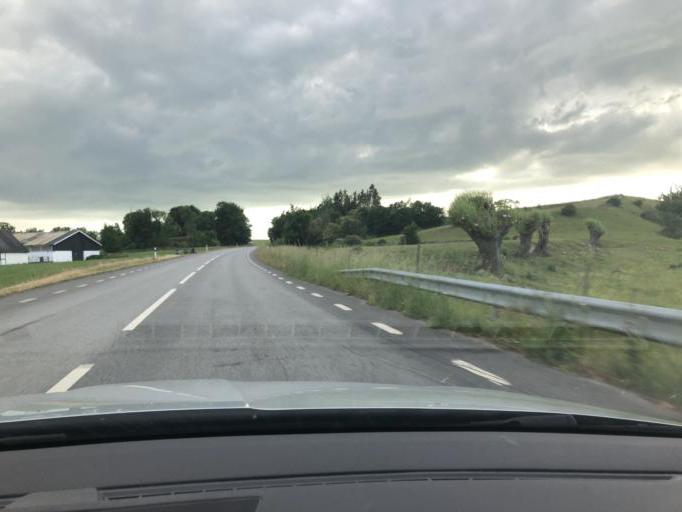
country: SE
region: Skane
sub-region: Simrishamns Kommun
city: Simrishamn
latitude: 55.5319
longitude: 14.2698
